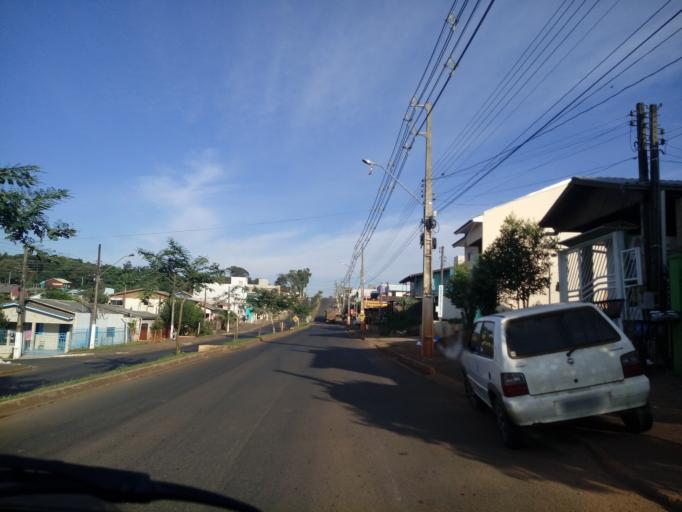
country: BR
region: Santa Catarina
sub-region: Chapeco
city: Chapeco
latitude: -27.0898
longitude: -52.6725
